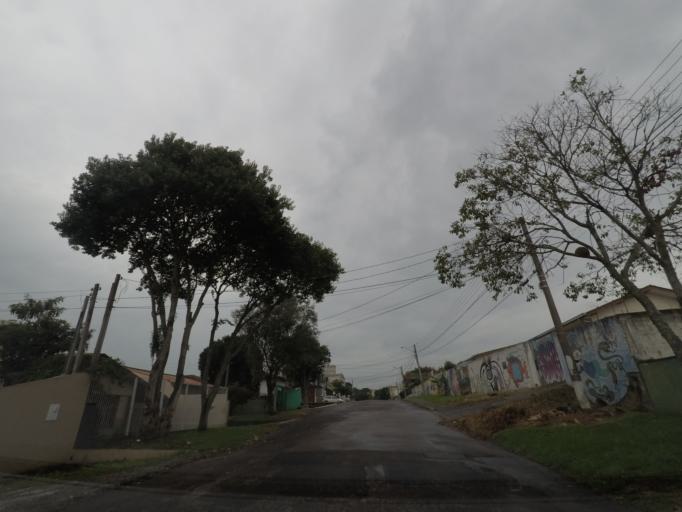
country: BR
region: Parana
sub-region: Curitiba
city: Curitiba
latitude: -25.4742
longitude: -49.3119
